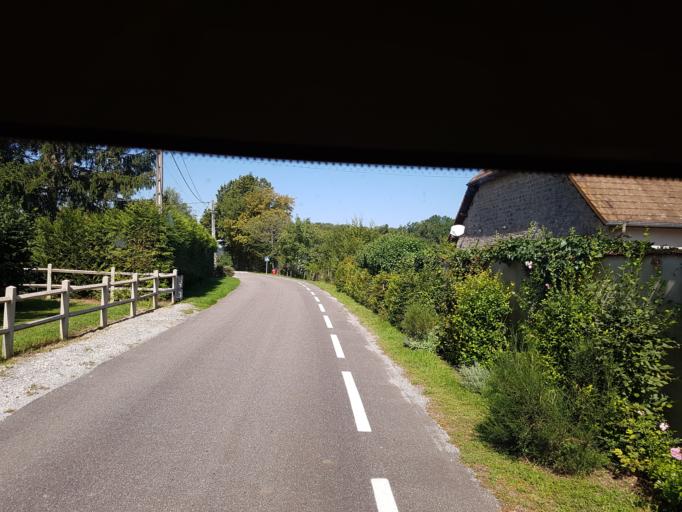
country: FR
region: Franche-Comte
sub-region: Departement du Jura
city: Perrigny
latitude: 46.7322
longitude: 5.5732
